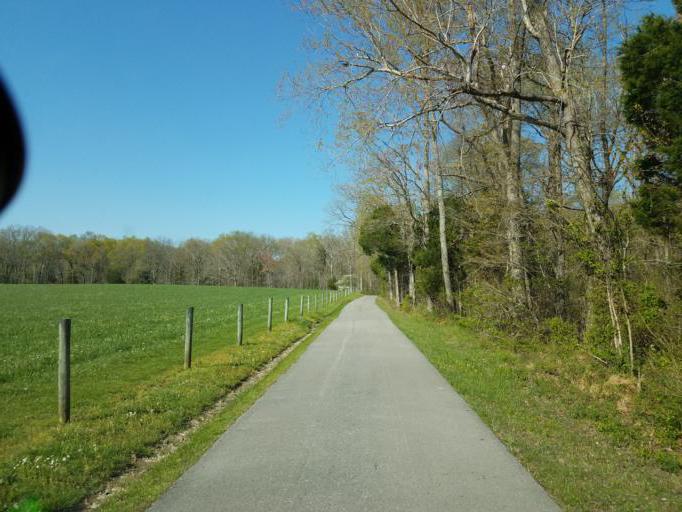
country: US
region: Kentucky
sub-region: Edmonson County
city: Brownsville
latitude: 37.1287
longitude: -86.1466
